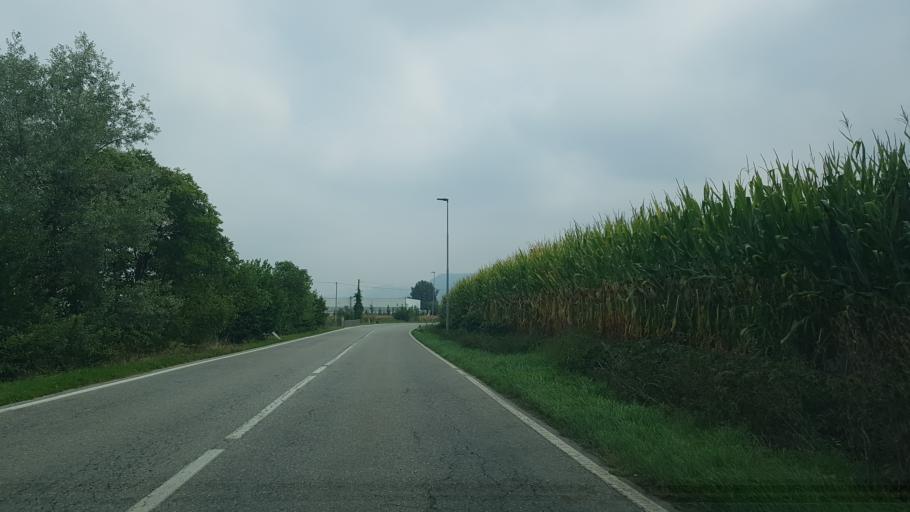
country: IT
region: Piedmont
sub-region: Provincia di Cuneo
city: Peveragno
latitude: 44.3304
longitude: 7.6293
